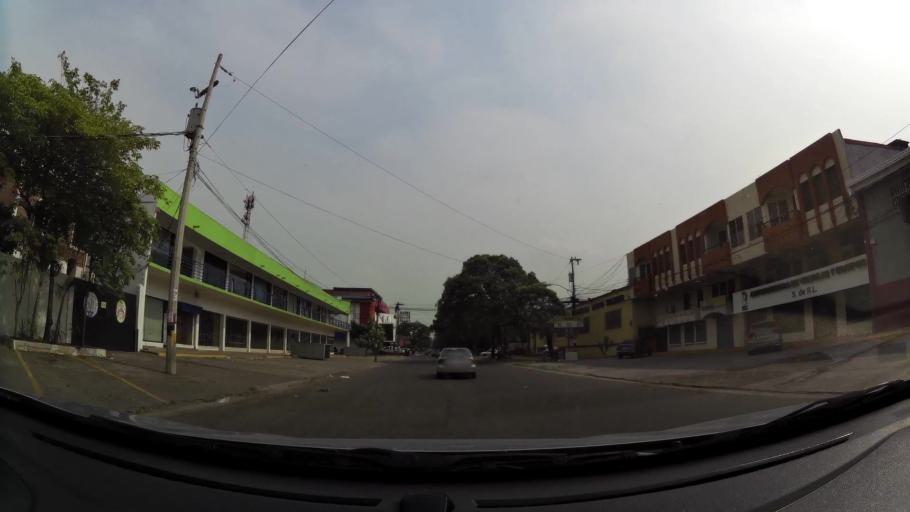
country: HN
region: Cortes
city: San Pedro Sula
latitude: 15.5178
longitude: -88.0234
